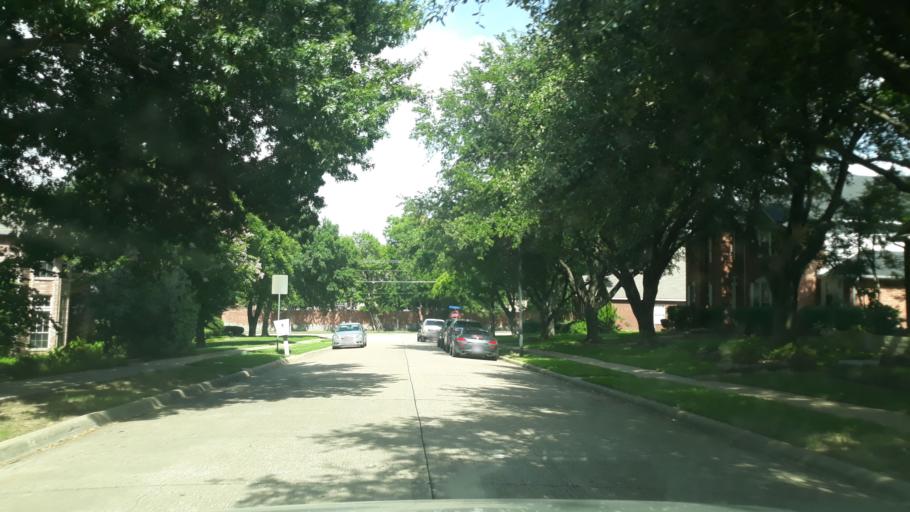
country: US
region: Texas
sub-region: Dallas County
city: Coppell
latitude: 32.9688
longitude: -97.0076
